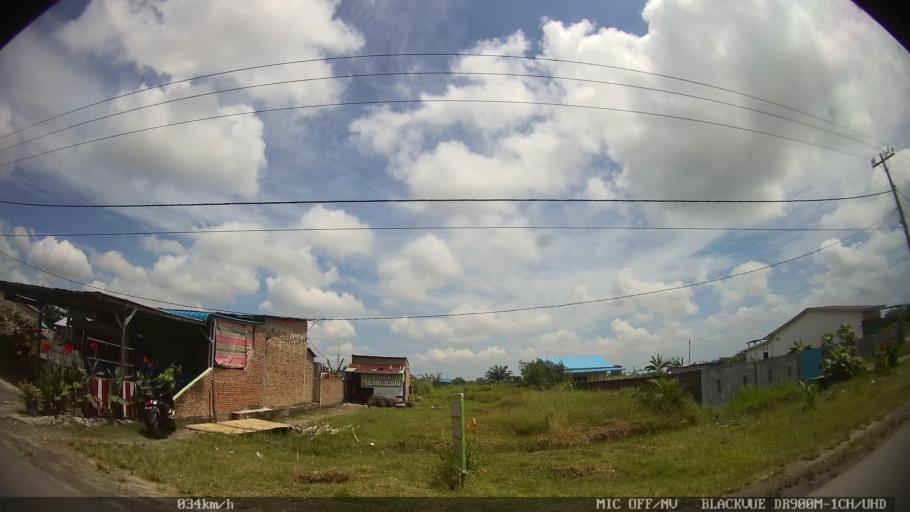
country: ID
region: North Sumatra
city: Percut
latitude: 3.6201
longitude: 98.7749
